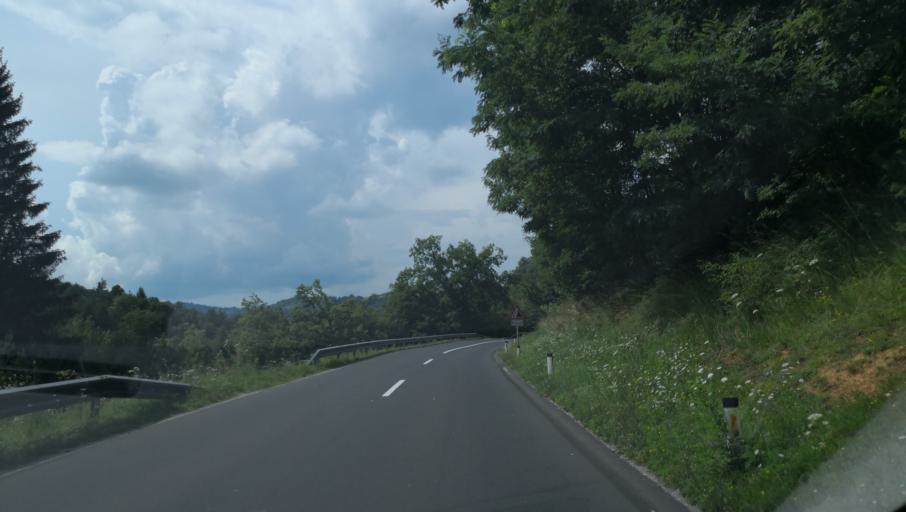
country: SI
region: Zuzemberk
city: Zuzemberk
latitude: 45.8442
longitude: 14.9063
